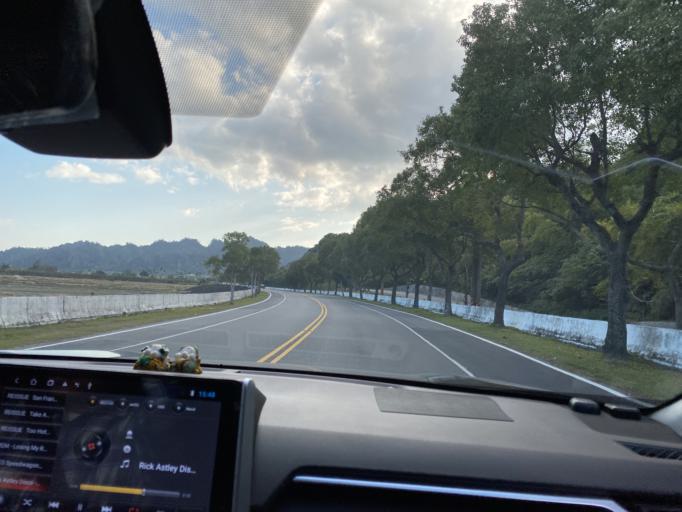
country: TW
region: Taiwan
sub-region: Taitung
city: Taitung
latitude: 22.9000
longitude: 121.1367
